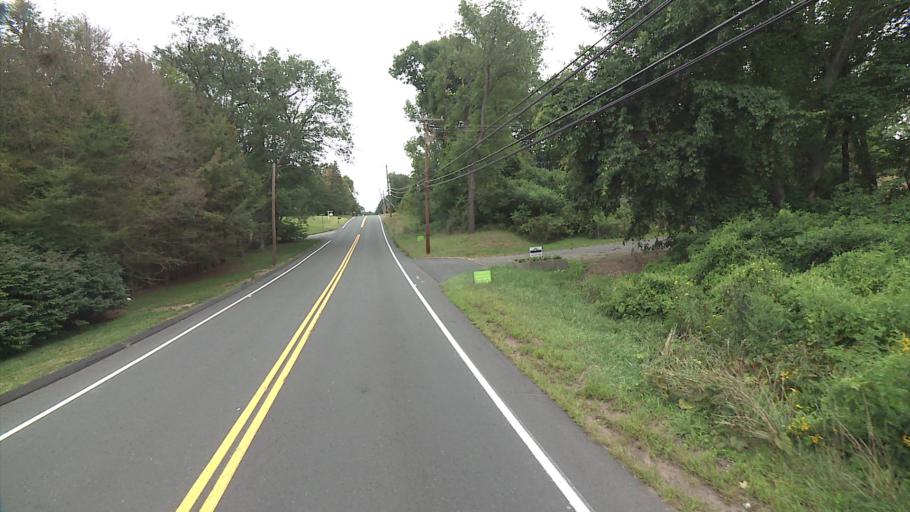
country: US
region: Connecticut
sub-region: Tolland County
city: Rockville
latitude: 41.8278
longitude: -72.4644
